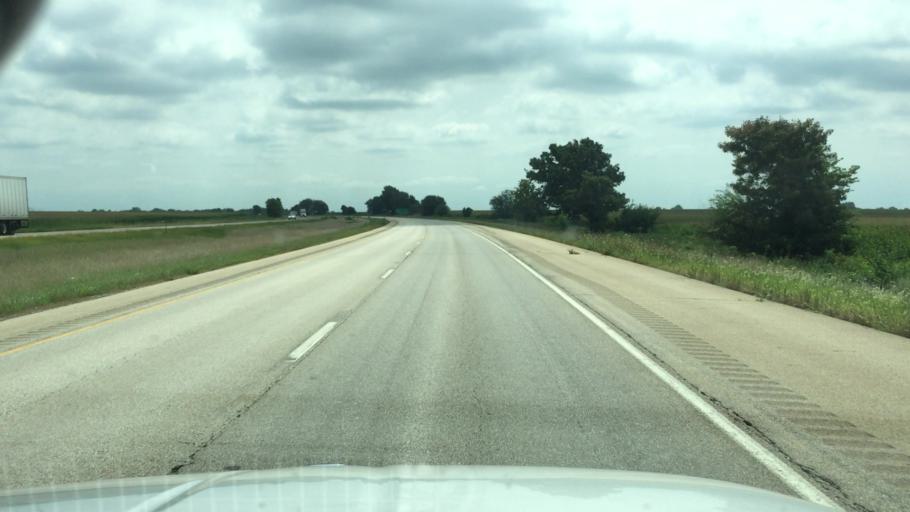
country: US
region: Illinois
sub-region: Knox County
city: Knoxville
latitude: 40.9050
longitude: -90.2371
